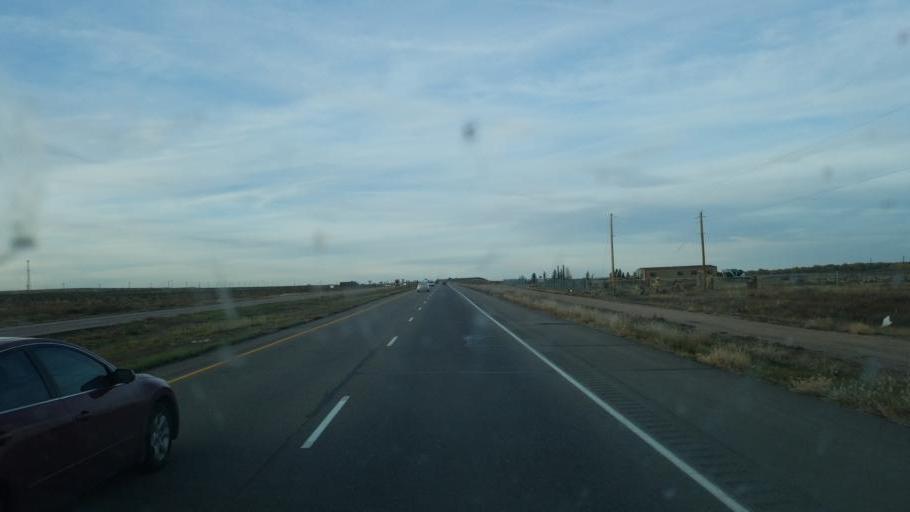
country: US
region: Colorado
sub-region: Pueblo County
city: Pueblo West
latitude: 38.3775
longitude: -104.6194
